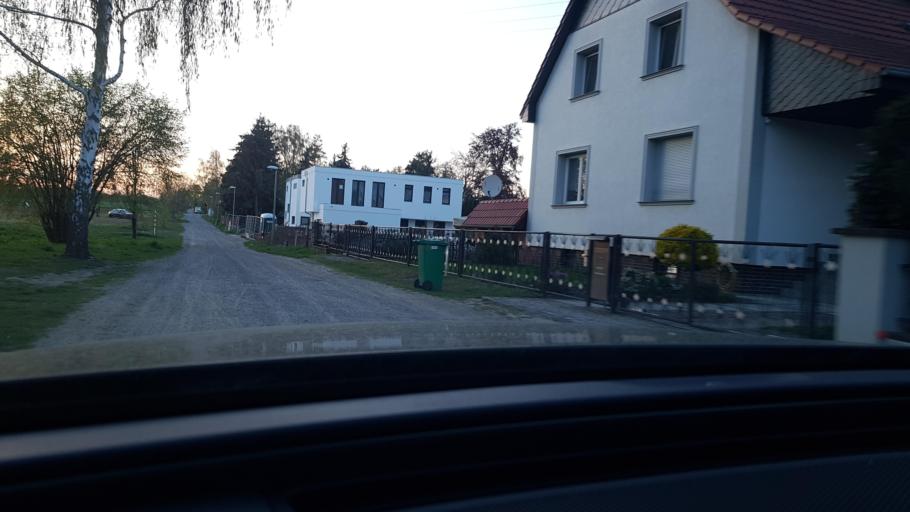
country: DE
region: Berlin
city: Lichtenrade
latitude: 52.3488
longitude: 13.4275
